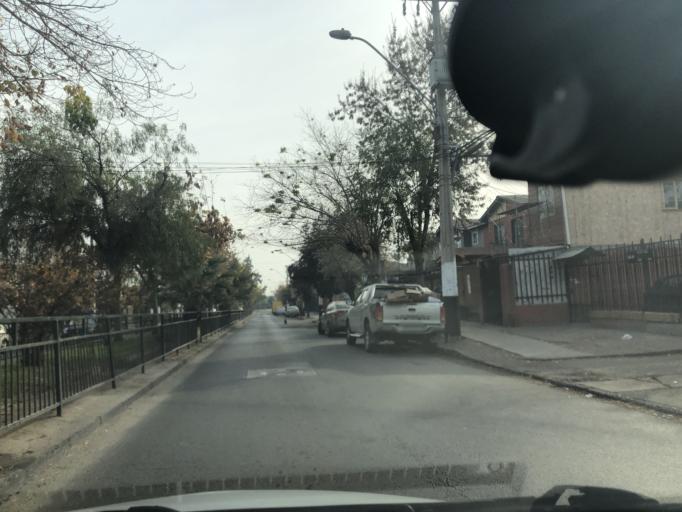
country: CL
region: Santiago Metropolitan
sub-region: Provincia de Cordillera
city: Puente Alto
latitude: -33.5817
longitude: -70.5558
